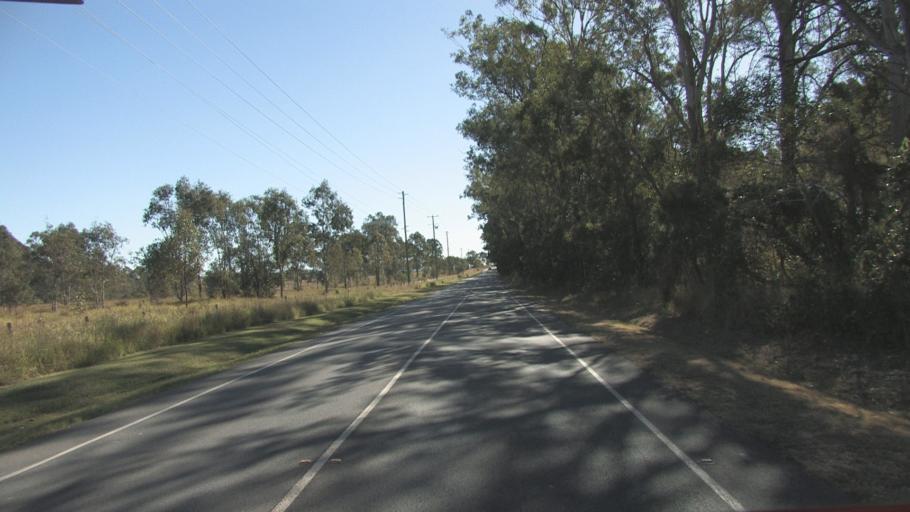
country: AU
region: Queensland
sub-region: Logan
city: North Maclean
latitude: -27.7736
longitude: 153.0071
